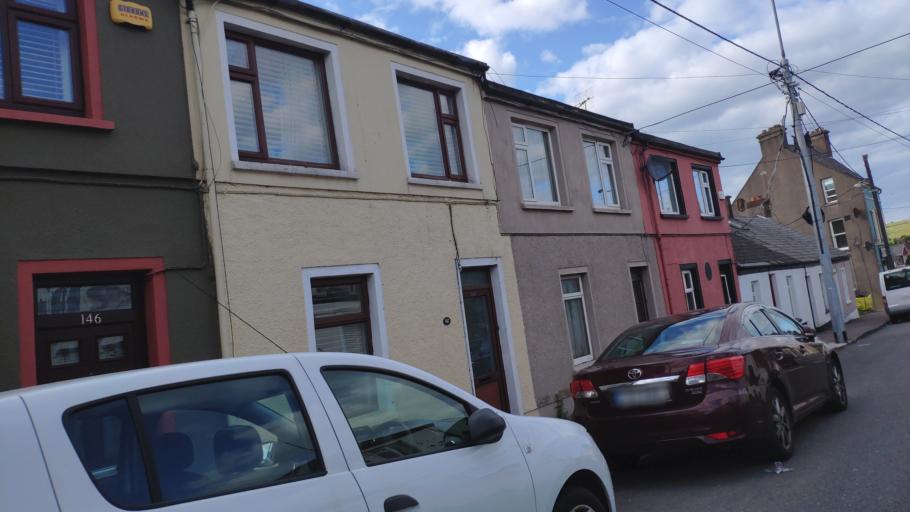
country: IE
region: Munster
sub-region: County Cork
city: Cork
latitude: 51.9092
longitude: -8.4549
